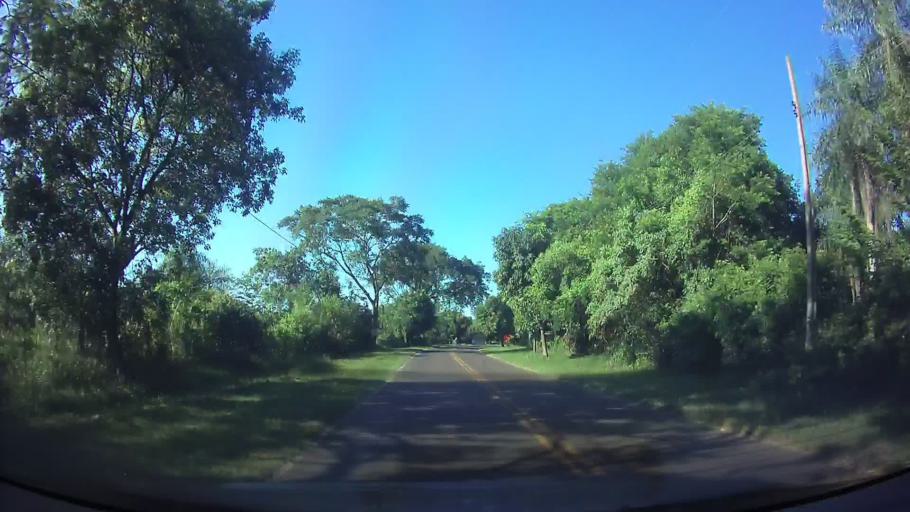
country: PY
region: Cordillera
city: Atyra
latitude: -25.2966
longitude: -57.1848
